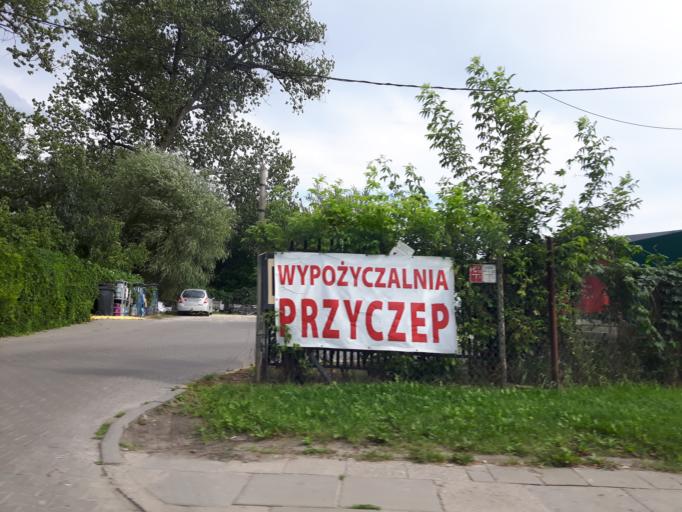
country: PL
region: Masovian Voivodeship
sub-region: Warszawa
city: Praga Poludnie
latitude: 52.2651
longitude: 21.0669
